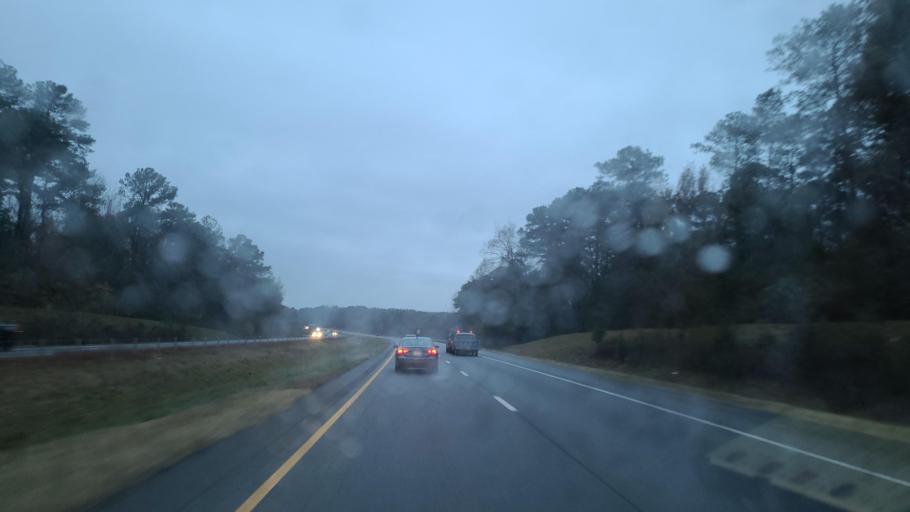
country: US
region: Alabama
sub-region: Hale County
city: Moundville
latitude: 32.9833
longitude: -87.7961
